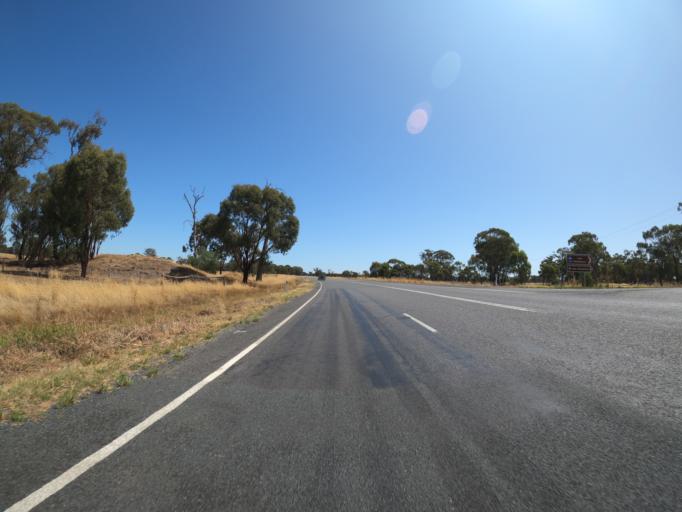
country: AU
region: New South Wales
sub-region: Corowa Shire
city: Corowa
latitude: -36.0638
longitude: 146.3963
